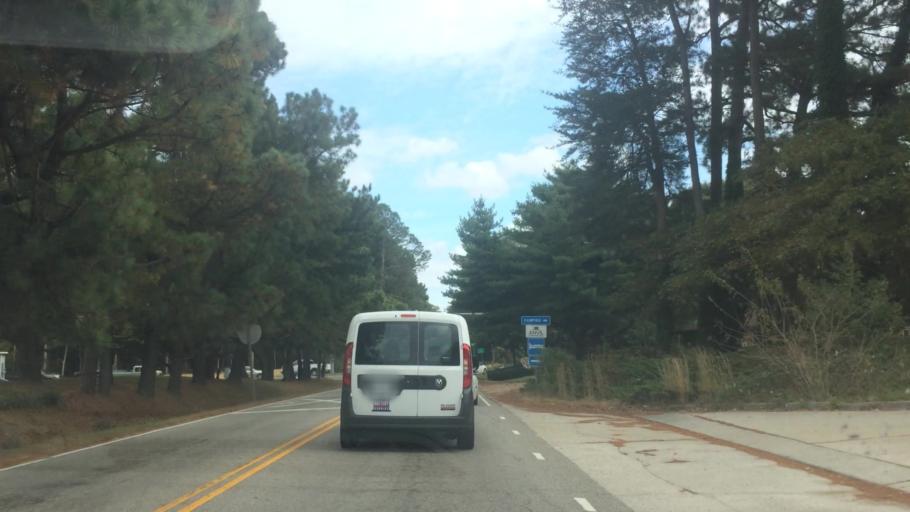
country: US
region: Virginia
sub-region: James City County
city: Williamsburg
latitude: 37.3128
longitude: -76.7308
